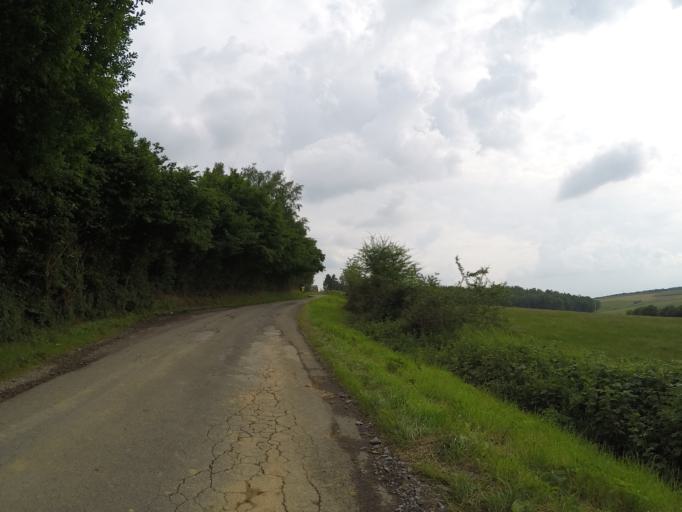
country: BE
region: Wallonia
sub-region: Province de Namur
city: Assesse
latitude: 50.3372
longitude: 5.0319
